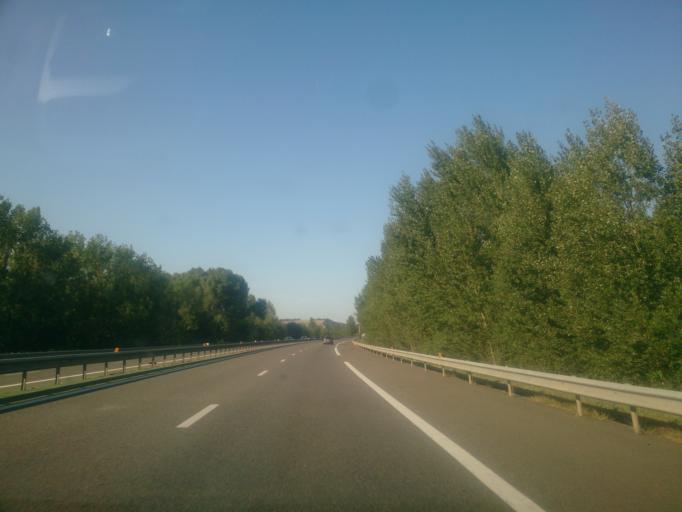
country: FR
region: Midi-Pyrenees
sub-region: Departement du Tarn-et-Garonne
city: Albias
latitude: 44.0855
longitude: 1.4214
